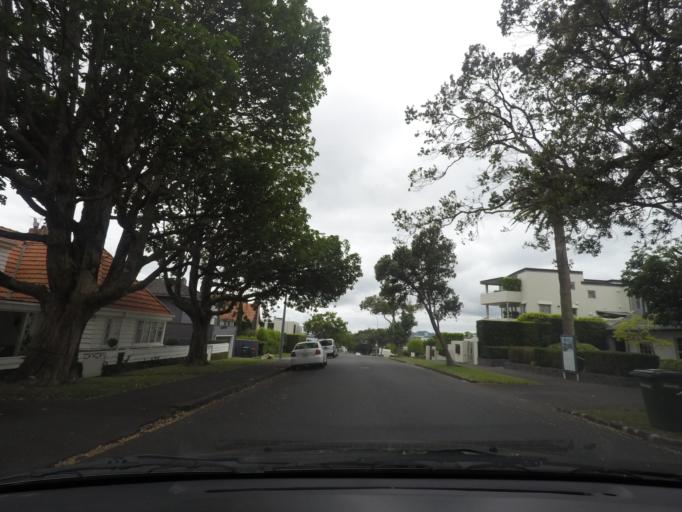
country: NZ
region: Auckland
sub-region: Auckland
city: Auckland
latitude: -36.8517
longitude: 174.7906
